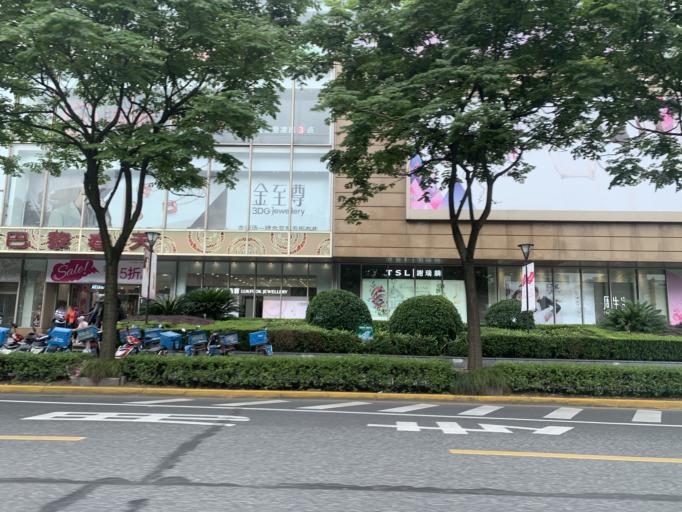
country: CN
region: Shanghai Shi
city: Pudong
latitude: 31.2110
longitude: 121.5156
